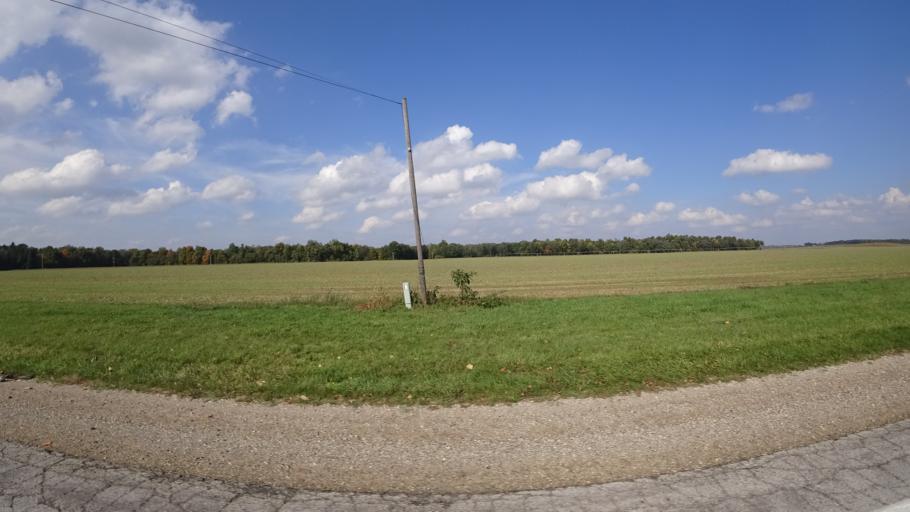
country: US
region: Michigan
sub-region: Saint Joseph County
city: Colon
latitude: 42.0101
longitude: -85.3771
